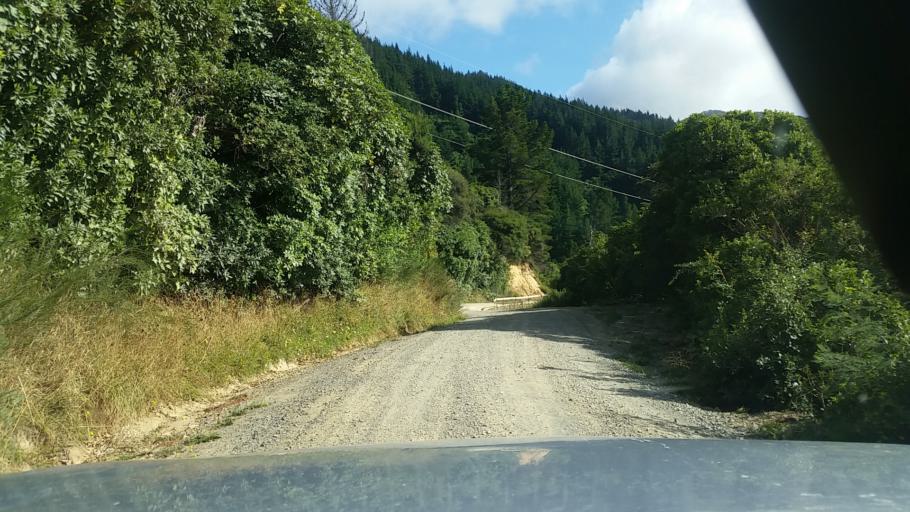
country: NZ
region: Marlborough
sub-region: Marlborough District
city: Picton
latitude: -41.2923
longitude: 174.1302
